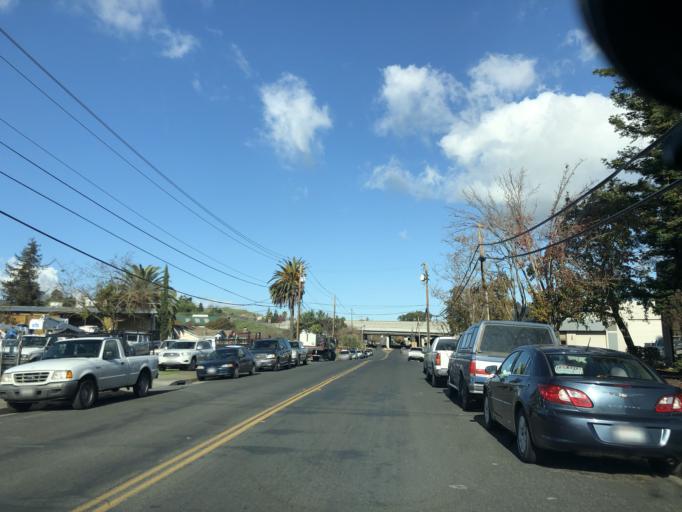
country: US
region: California
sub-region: Contra Costa County
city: Pacheco
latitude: 37.9958
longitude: -122.0743
